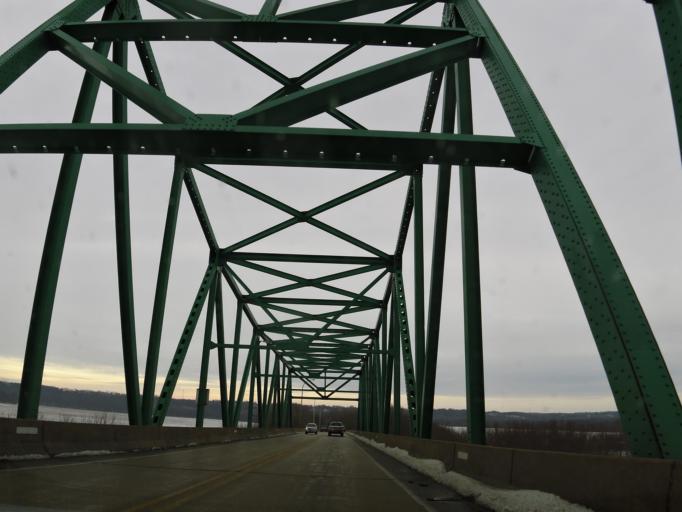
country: US
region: Illinois
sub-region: LaSalle County
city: Peru
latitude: 41.3234
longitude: -89.1199
